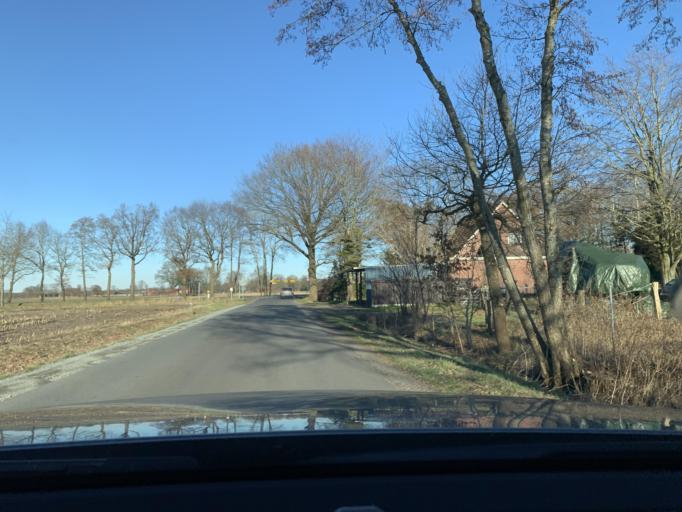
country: DE
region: Lower Saxony
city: Hatten
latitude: 53.0692
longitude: 8.3024
